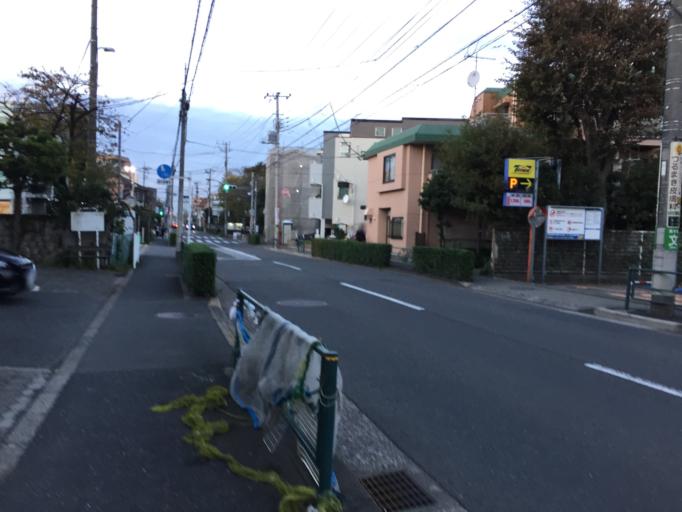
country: JP
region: Tokyo
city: Tokyo
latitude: 35.6379
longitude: 139.6438
